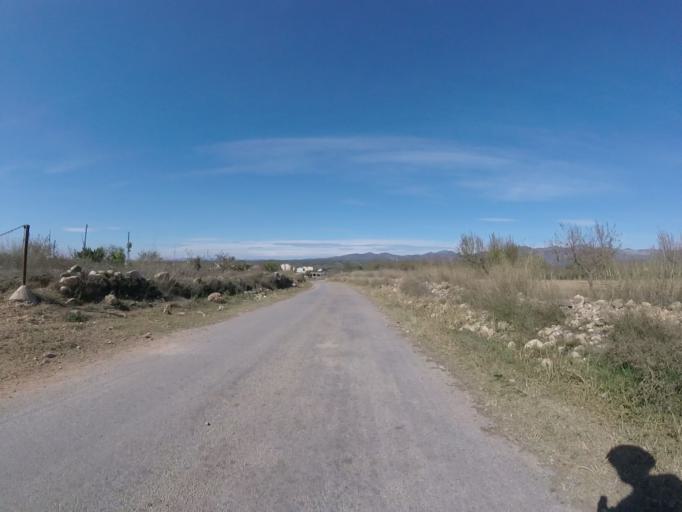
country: ES
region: Valencia
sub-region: Provincia de Castello
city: Benlloch
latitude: 40.2112
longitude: 0.0366
